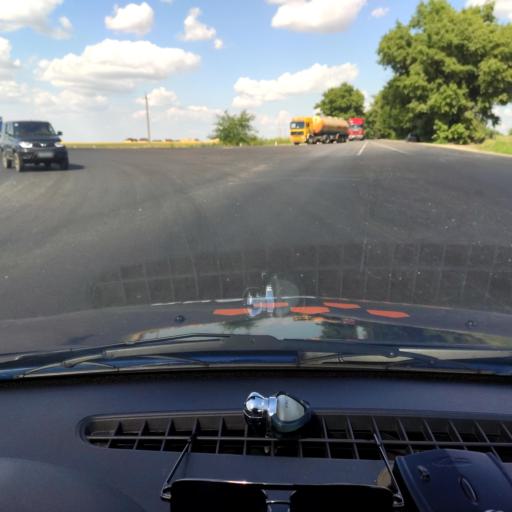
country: RU
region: Voronezj
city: Novovoronezh
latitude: 51.3421
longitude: 39.2769
